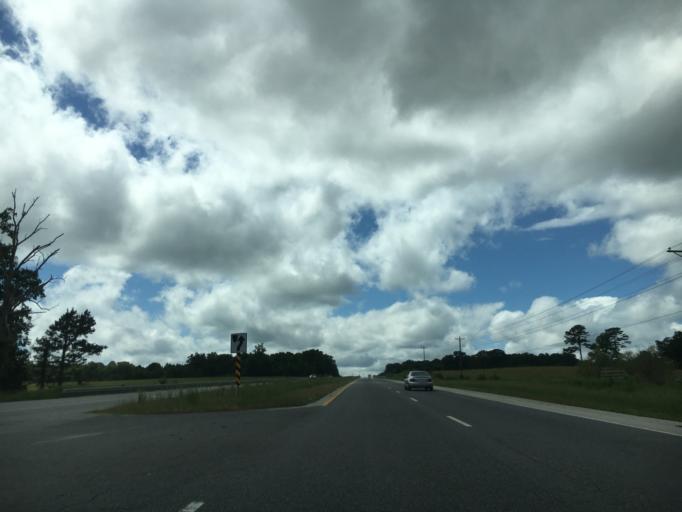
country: US
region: Virginia
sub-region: Mecklenburg County
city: Boydton
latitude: 36.6716
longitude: -78.2762
